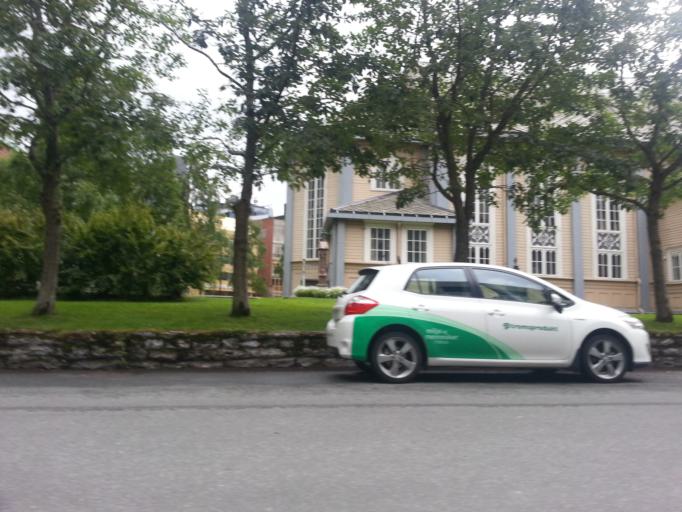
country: NO
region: Troms
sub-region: Tromso
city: Tromso
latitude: 69.6488
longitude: 18.9571
